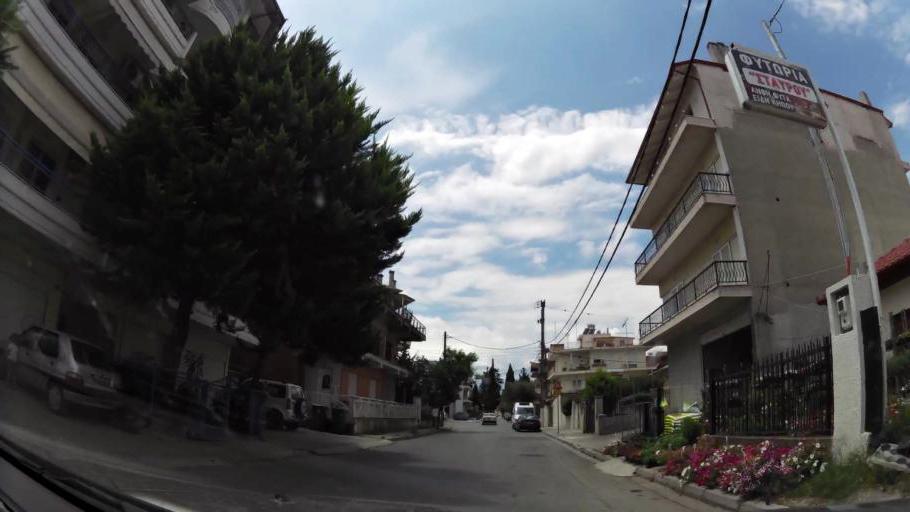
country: GR
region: Central Macedonia
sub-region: Nomos Pierias
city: Katerini
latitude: 40.2664
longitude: 22.5154
